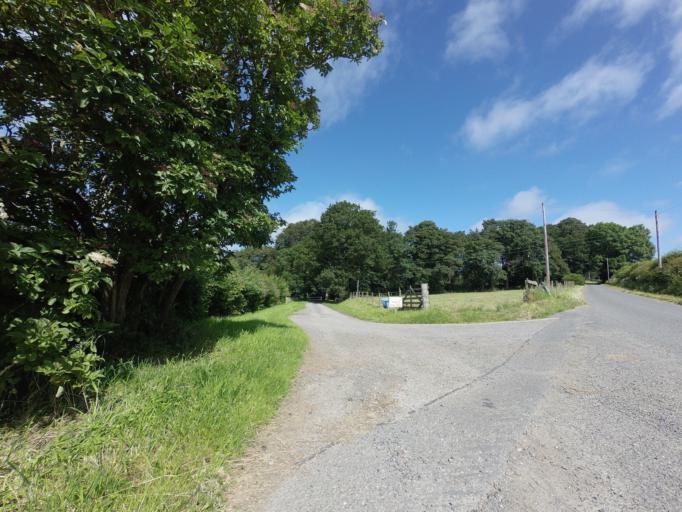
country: GB
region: Scotland
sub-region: Aberdeenshire
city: Turriff
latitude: 57.5824
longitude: -2.5069
